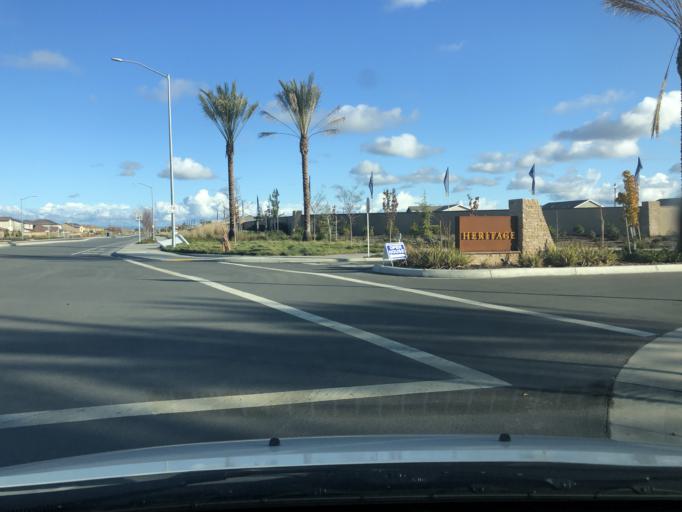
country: US
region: California
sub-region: Sacramento County
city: Antelope
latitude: 38.7752
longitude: -121.3925
